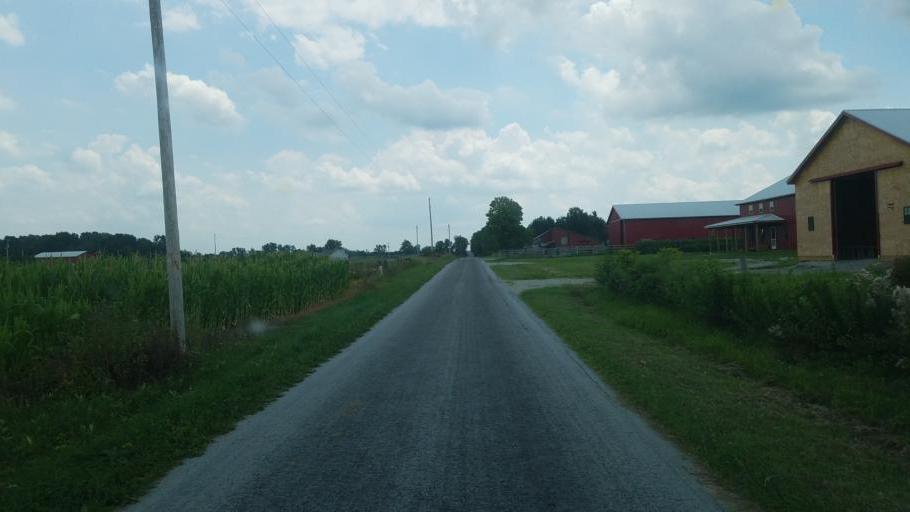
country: US
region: Ohio
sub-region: Hardin County
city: Kenton
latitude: 40.5639
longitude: -83.4869
